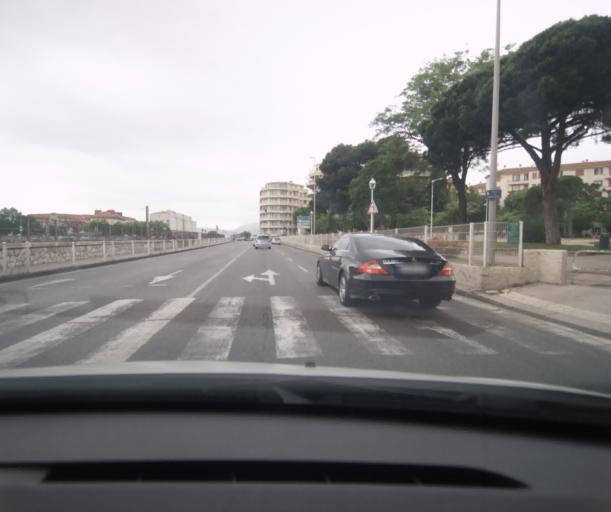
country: FR
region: Provence-Alpes-Cote d'Azur
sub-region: Departement du Var
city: Toulon
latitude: 43.1295
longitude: 5.9282
